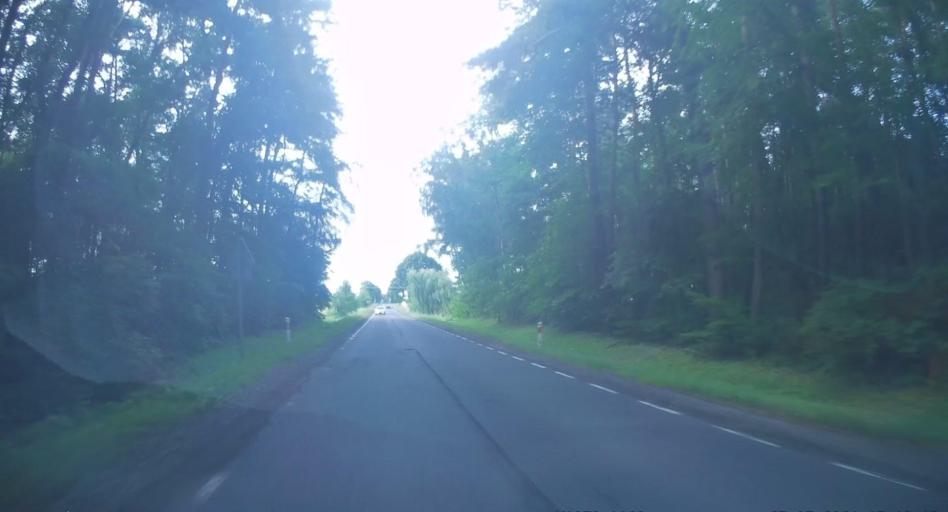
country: PL
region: Lodz Voivodeship
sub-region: Powiat rawski
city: Rawa Mazowiecka
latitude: 51.6856
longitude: 20.2675
